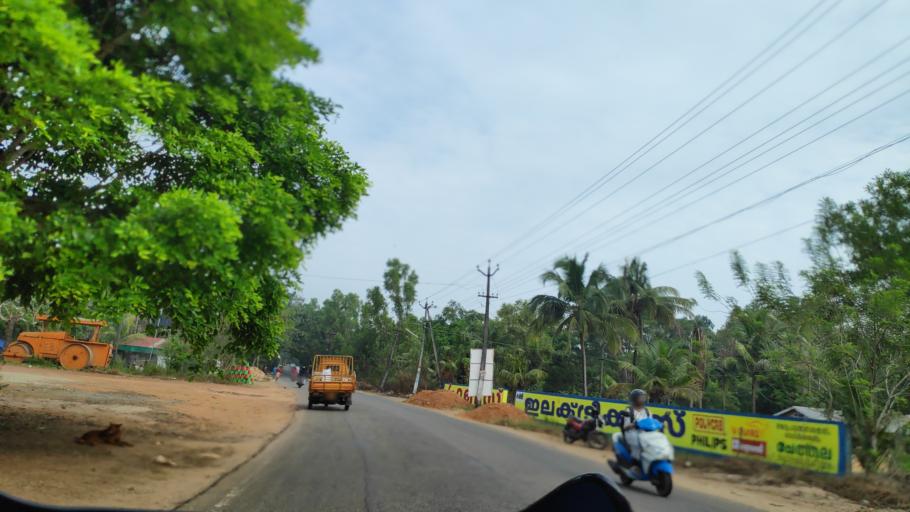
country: IN
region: Kerala
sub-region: Alappuzha
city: Vayalar
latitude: 9.7225
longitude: 76.3606
